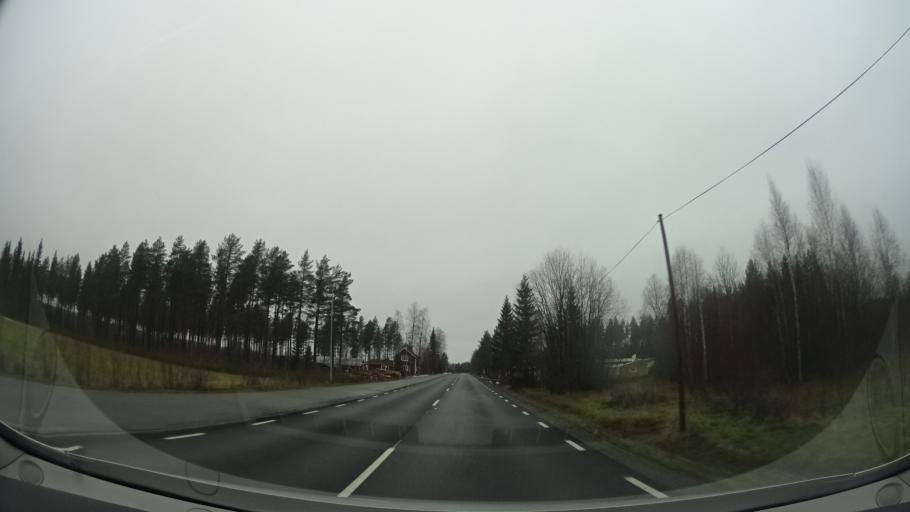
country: SE
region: Vaesterbotten
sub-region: Skelleftea Kommun
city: Kage
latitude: 64.8387
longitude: 20.9433
